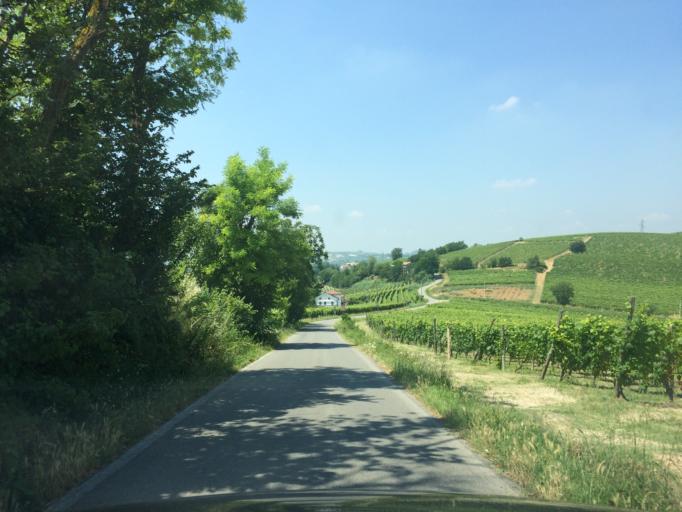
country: IT
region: Piedmont
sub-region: Provincia di Asti
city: Vaglio Serra
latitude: 44.7794
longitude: 8.3148
